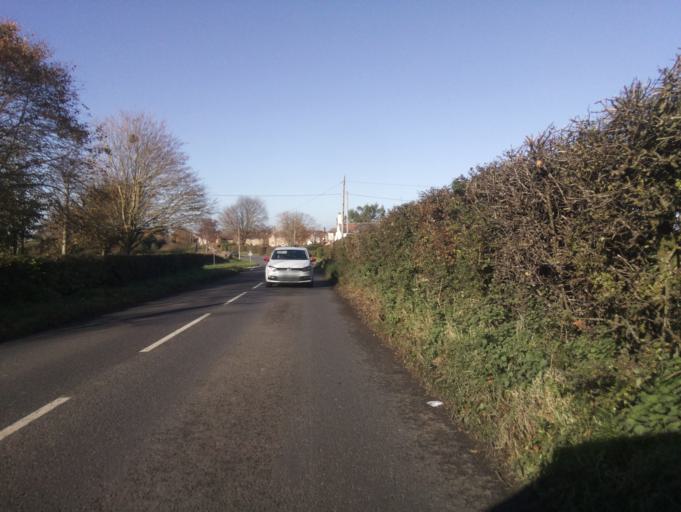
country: GB
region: England
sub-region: Somerset
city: Ilchester
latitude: 50.9639
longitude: -2.6757
